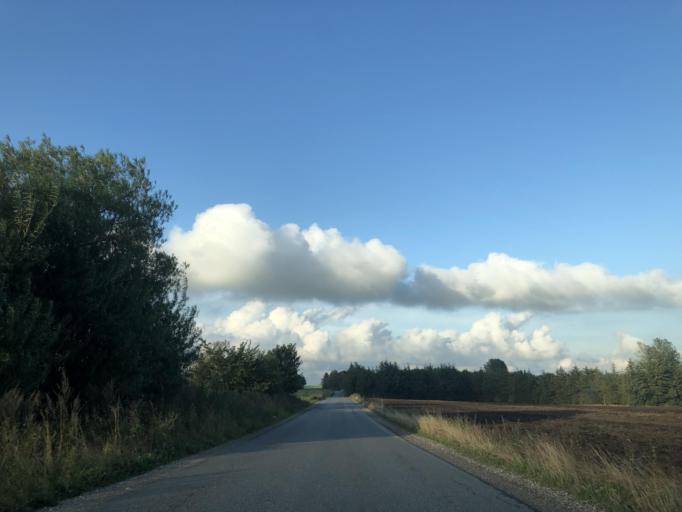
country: DK
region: North Denmark
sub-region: Rebild Kommune
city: Stovring
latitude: 56.9182
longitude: 9.7563
